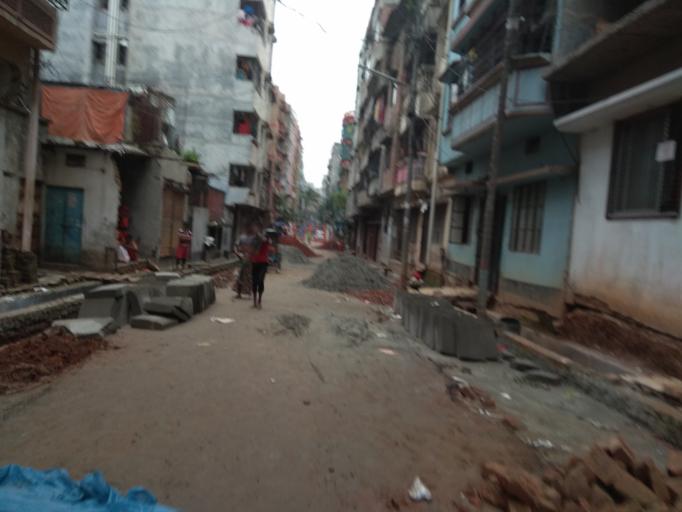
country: BD
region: Dhaka
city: Tungi
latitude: 23.8246
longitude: 90.3750
